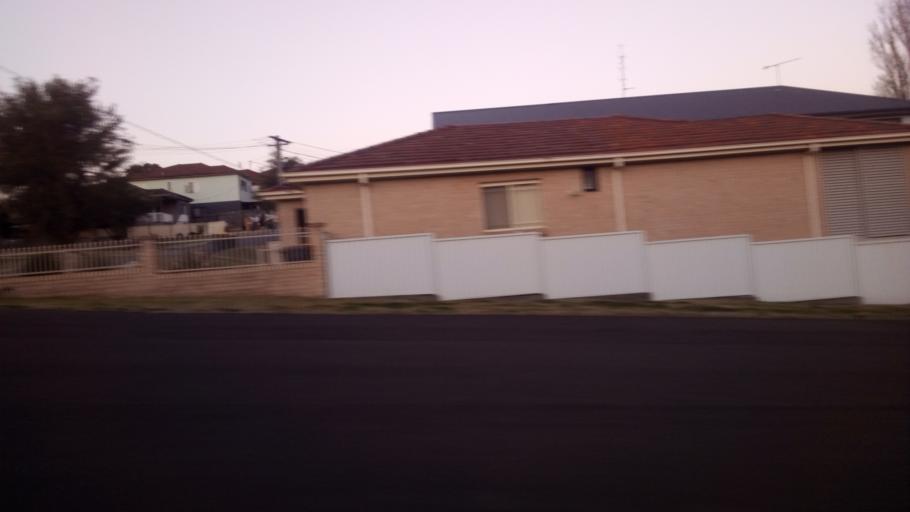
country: AU
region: New South Wales
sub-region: Wollongong
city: Cringila
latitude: -34.4707
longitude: 150.8686
